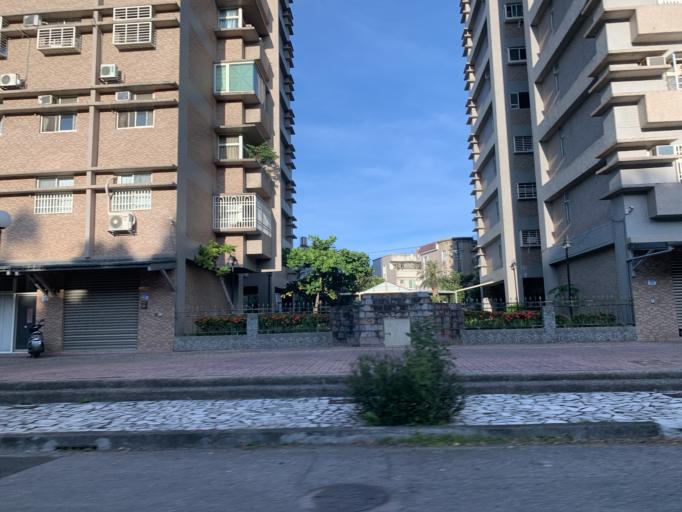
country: TW
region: Taiwan
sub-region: Hualien
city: Hualian
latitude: 24.0041
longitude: 121.6295
